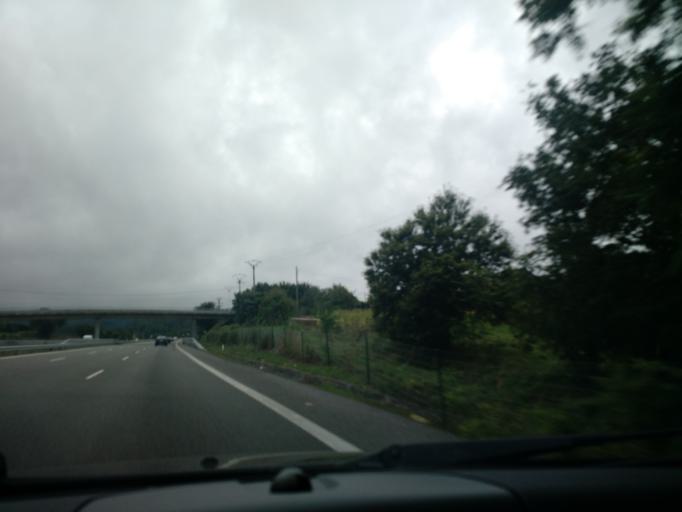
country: ES
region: Galicia
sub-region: Provincia da Coruna
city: Abegondo
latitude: 43.2053
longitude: -8.2880
